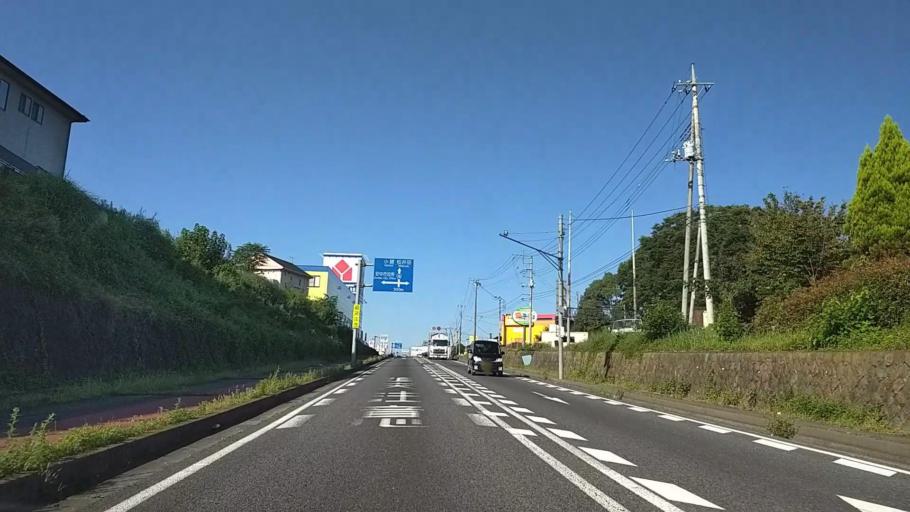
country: JP
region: Gunma
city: Annaka
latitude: 36.3294
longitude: 138.8907
